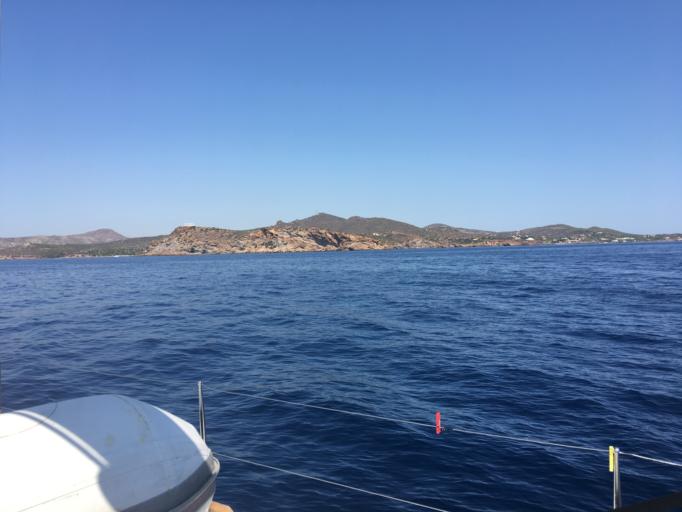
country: GR
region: Attica
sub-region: Nomarchia Anatolikis Attikis
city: Lavrio
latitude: 37.6382
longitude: 24.0333
